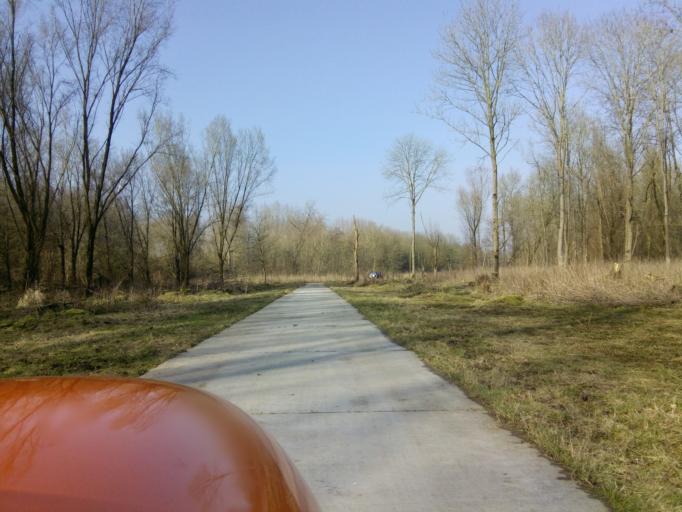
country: NL
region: Gelderland
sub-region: Gemeente Nijkerk
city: Nijkerk
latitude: 52.2887
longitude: 5.4633
